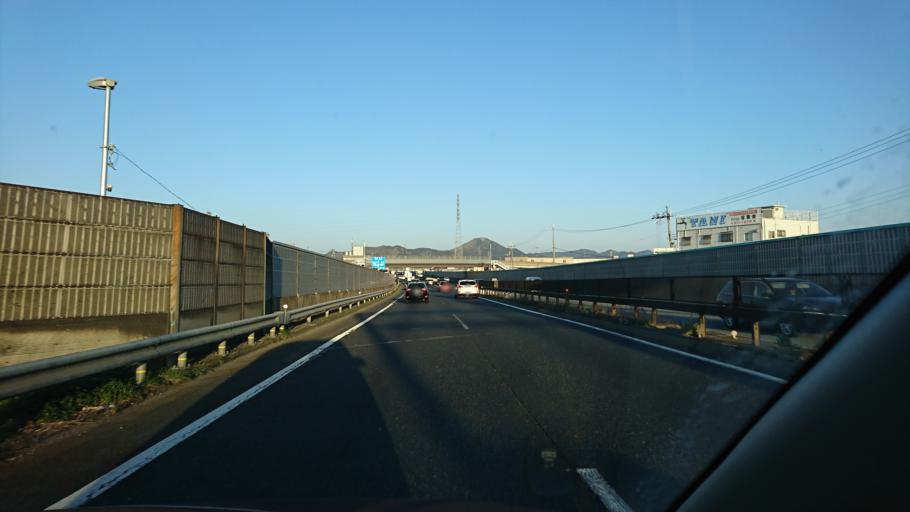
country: JP
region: Hyogo
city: Kakogawacho-honmachi
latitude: 34.7825
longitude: 134.8309
